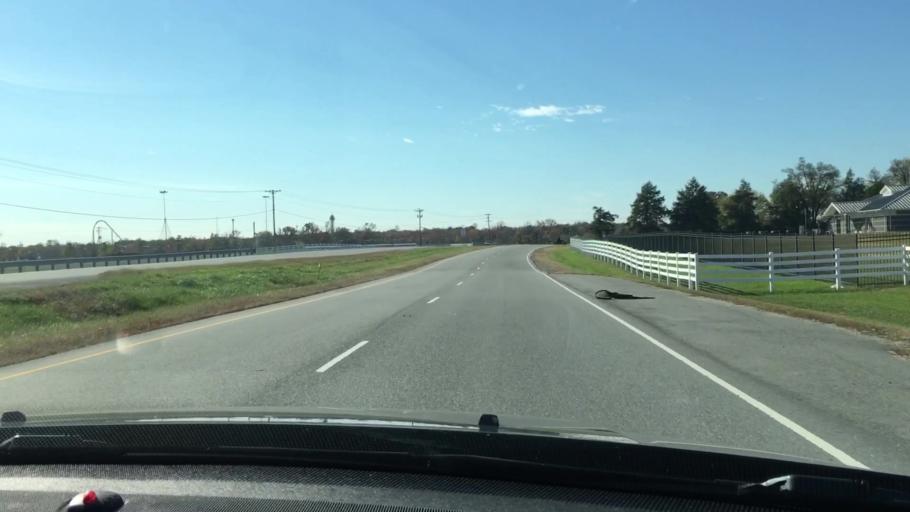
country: US
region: Virginia
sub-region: Hanover County
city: Hanover
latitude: 37.8503
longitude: -77.4181
